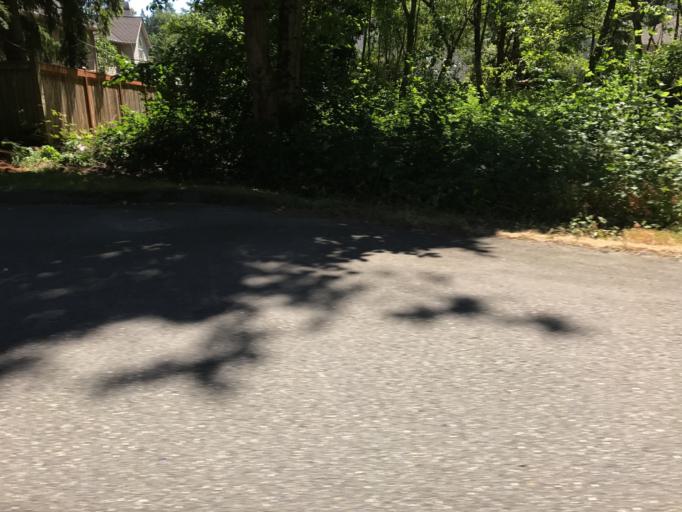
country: US
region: Washington
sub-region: King County
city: Redmond
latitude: 47.6397
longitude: -122.1211
